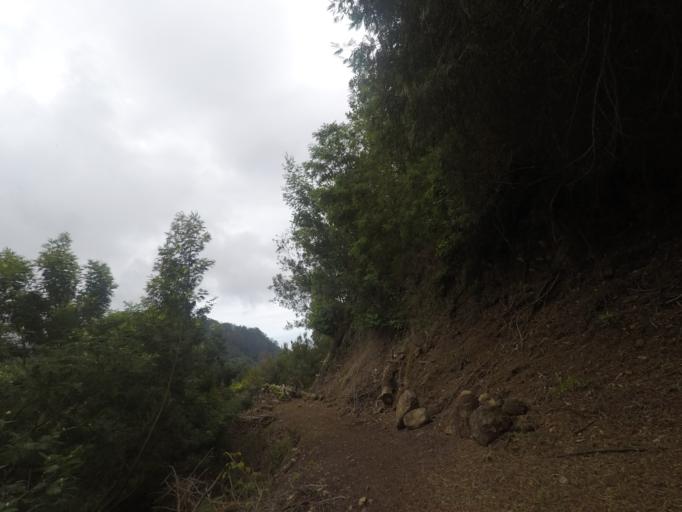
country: PT
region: Madeira
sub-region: Santana
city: Santana
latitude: 32.7548
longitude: -16.8749
